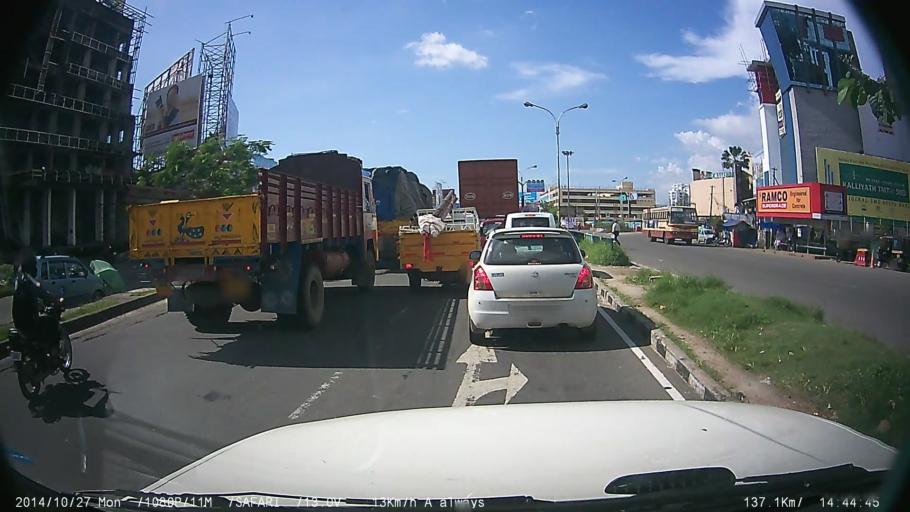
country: IN
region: Kerala
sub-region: Ernakulam
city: Elur
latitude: 10.0234
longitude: 76.3089
